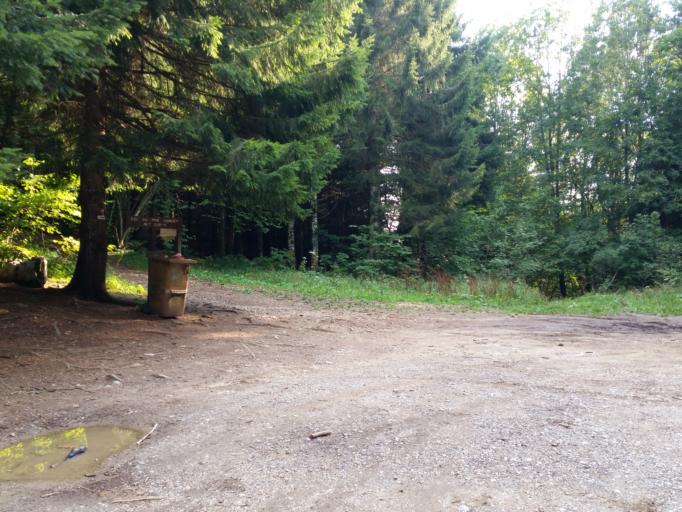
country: FR
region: Rhone-Alpes
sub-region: Departement de la Haute-Savoie
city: Veyrier-du-Lac
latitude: 45.9083
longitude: 6.1726
